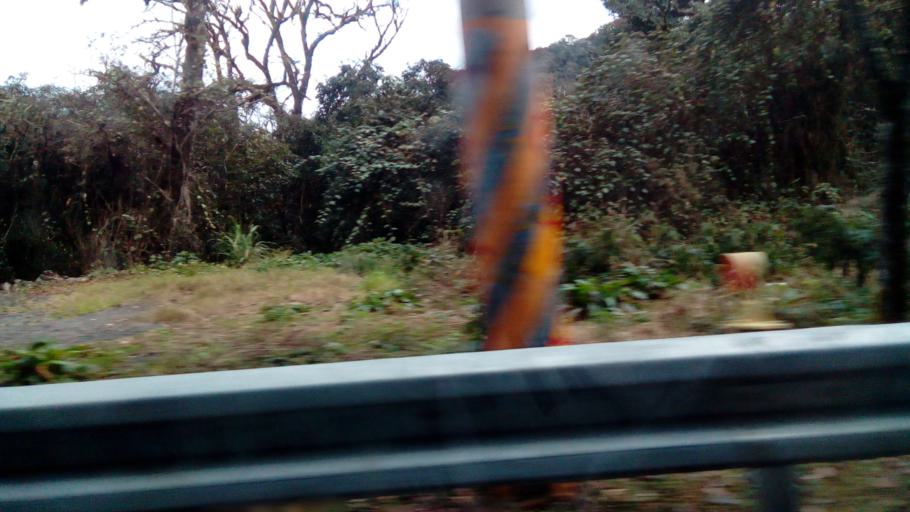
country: TW
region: Taiwan
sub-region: Hualien
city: Hualian
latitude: 24.3994
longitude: 121.3651
